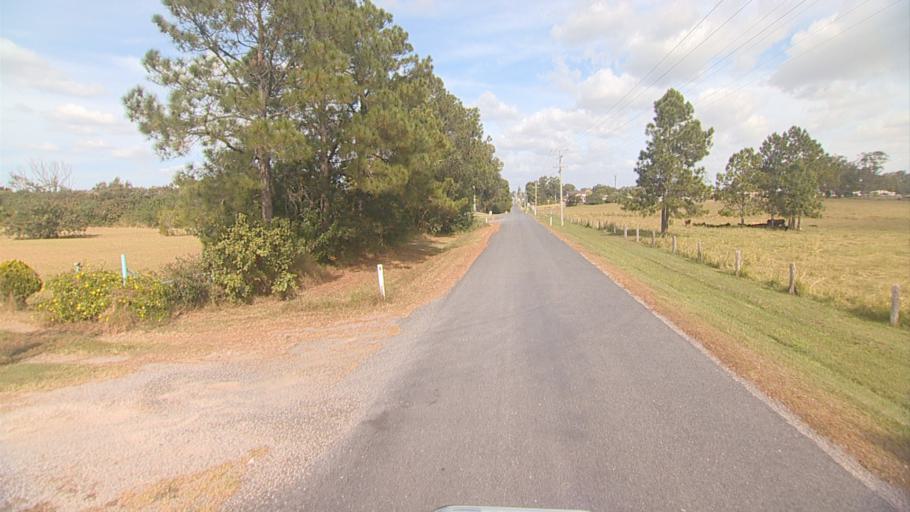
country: AU
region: Queensland
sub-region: Logan
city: Waterford West
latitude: -27.6795
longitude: 153.1590
